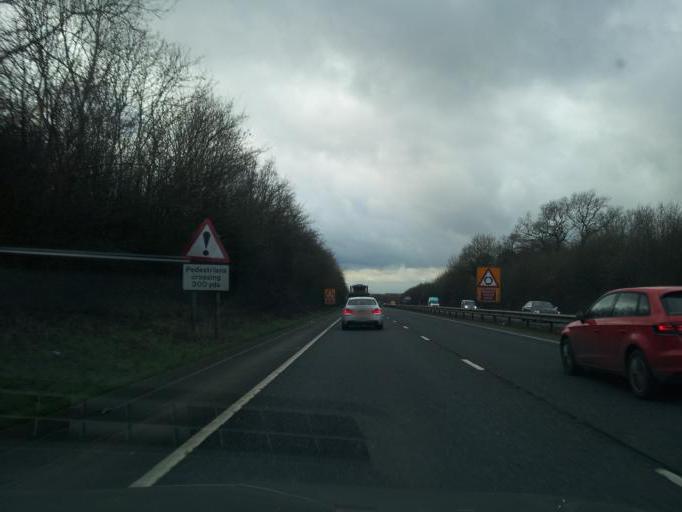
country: GB
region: England
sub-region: Norfolk
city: Costessey
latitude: 52.6547
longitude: 1.1578
